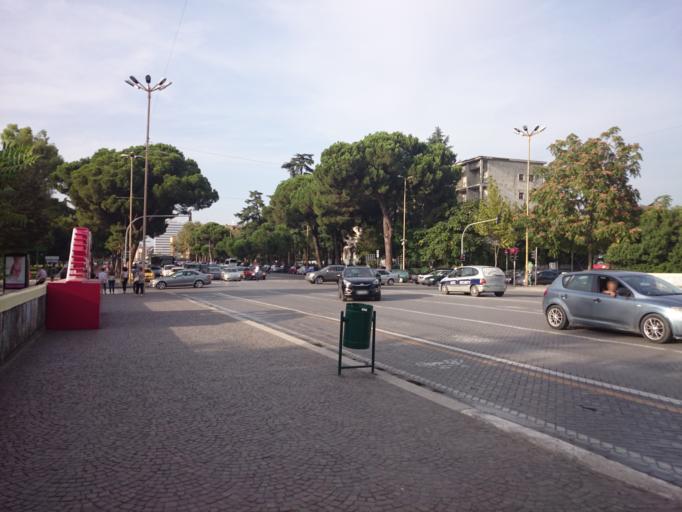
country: AL
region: Tirane
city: Tirana
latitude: 41.3236
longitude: 19.8195
